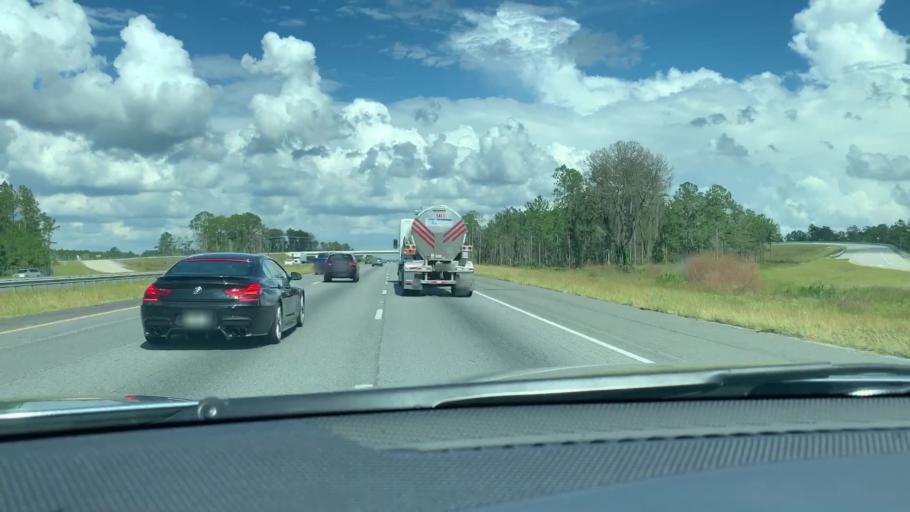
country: US
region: Georgia
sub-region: Camden County
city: Woodbine
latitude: 31.0532
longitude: -81.6426
